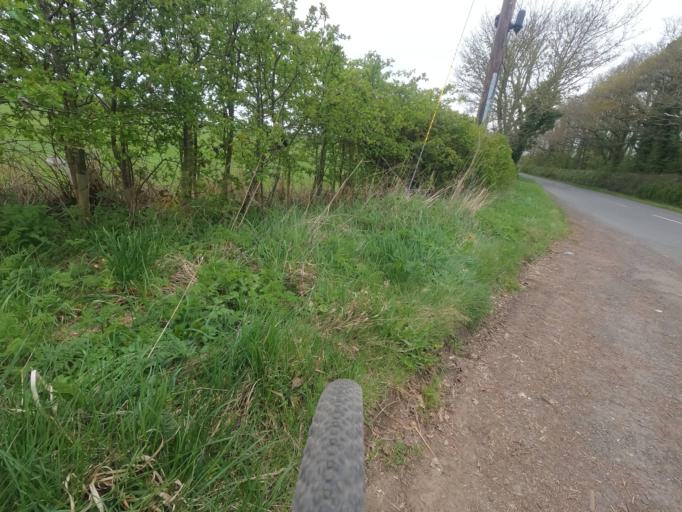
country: GB
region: England
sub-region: Northumberland
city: Ponteland
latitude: 55.0836
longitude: -1.7641
